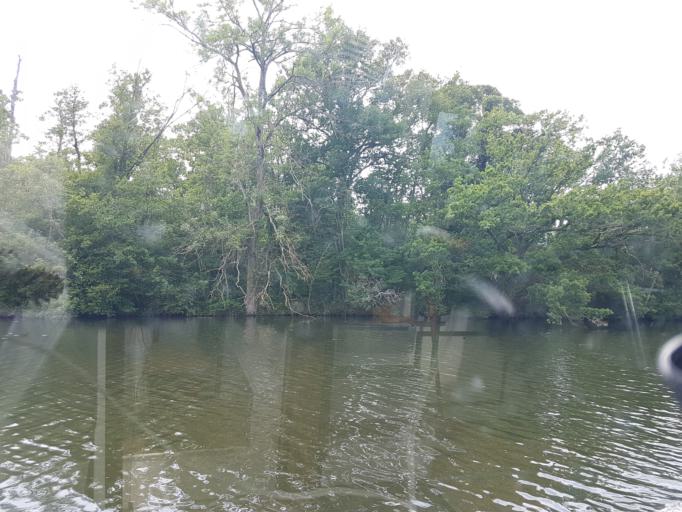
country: FR
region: Bourgogne
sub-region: Departement de l'Yonne
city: Gurgy
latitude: 47.8616
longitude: 3.5522
